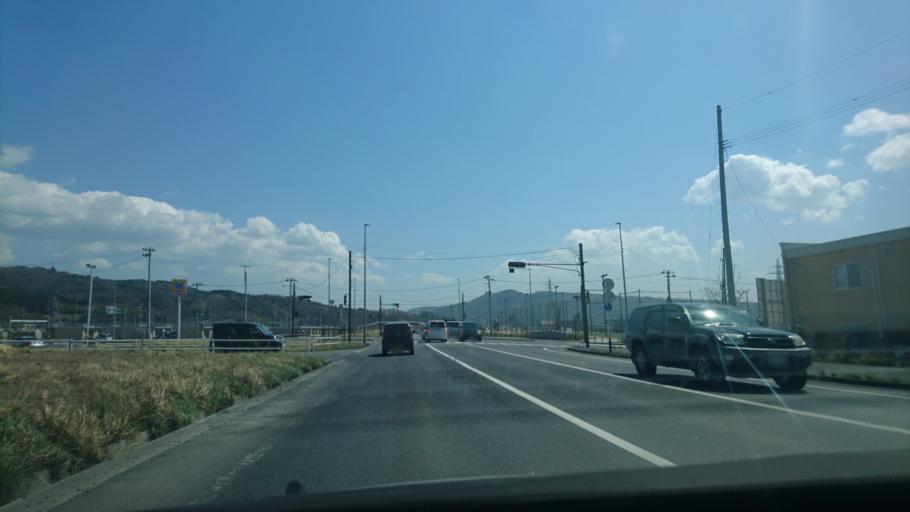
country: JP
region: Miyagi
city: Ishinomaki
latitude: 38.4559
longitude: 141.3013
